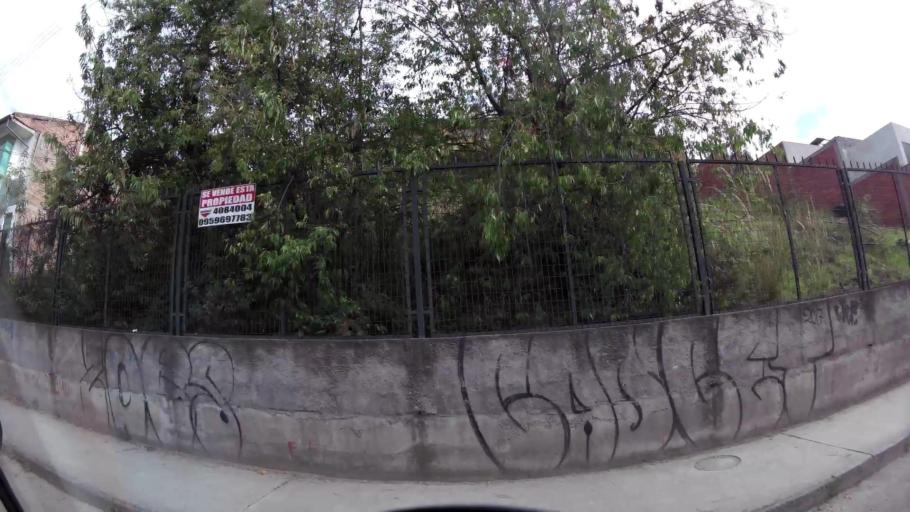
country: EC
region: Azuay
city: Cuenca
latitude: -2.8818
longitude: -78.9768
